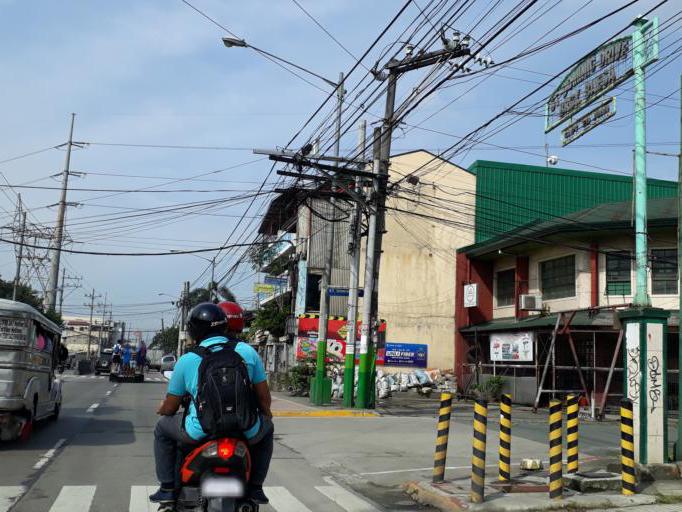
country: PH
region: Calabarzon
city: Bagong Pagasa
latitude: 14.6729
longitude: 121.0128
